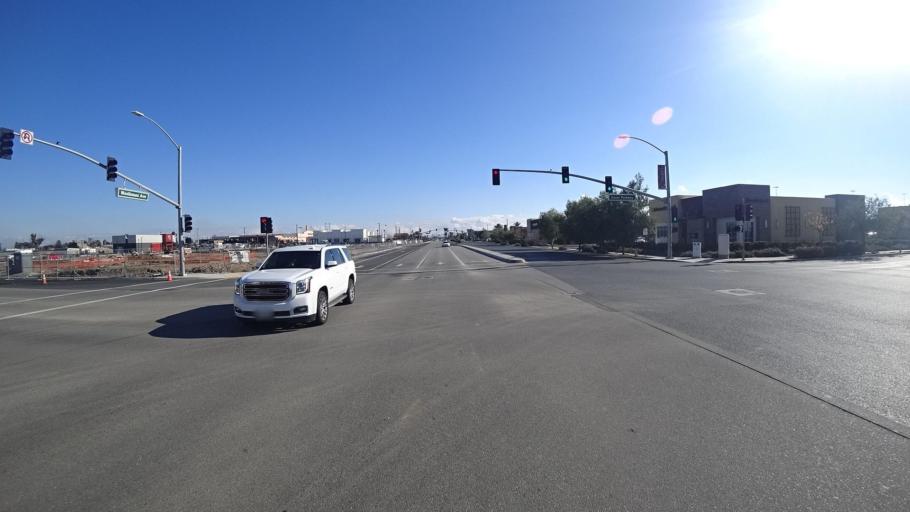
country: US
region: California
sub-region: Kern County
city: Delano
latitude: 35.7469
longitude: -119.2496
